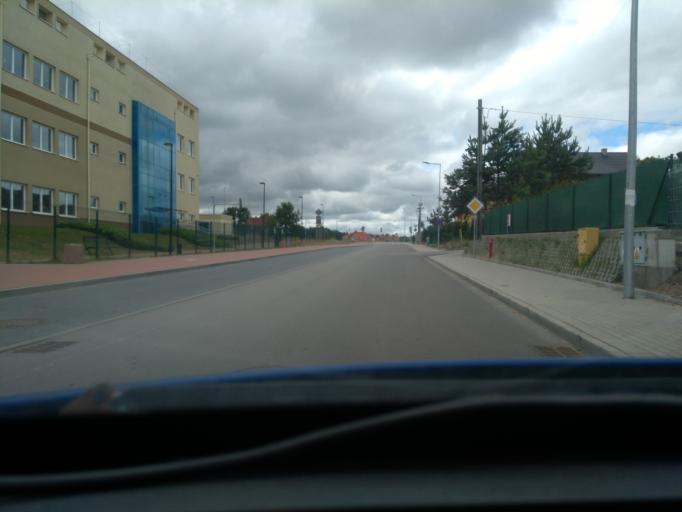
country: PL
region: Pomeranian Voivodeship
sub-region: Powiat kartuski
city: Banino
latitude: 54.3962
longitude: 18.4002
